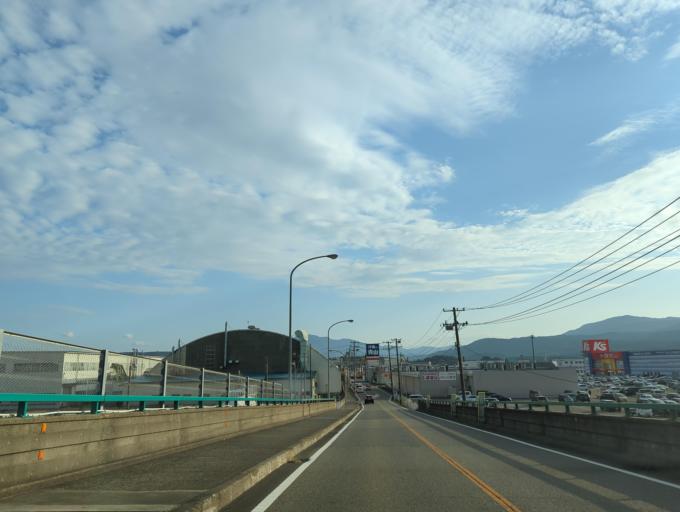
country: JP
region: Niigata
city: Kashiwazaki
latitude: 37.3644
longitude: 138.5635
